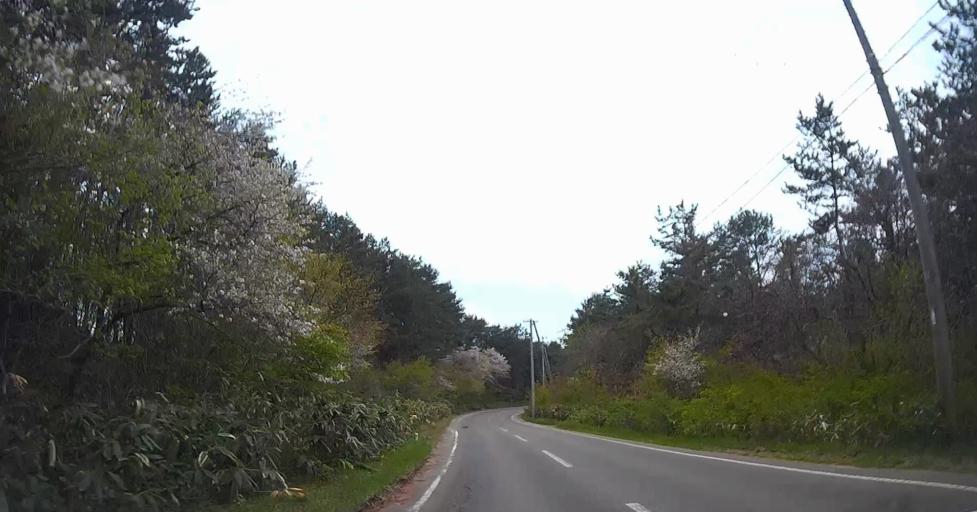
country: JP
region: Aomori
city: Shimokizukuri
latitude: 40.9367
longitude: 140.3365
